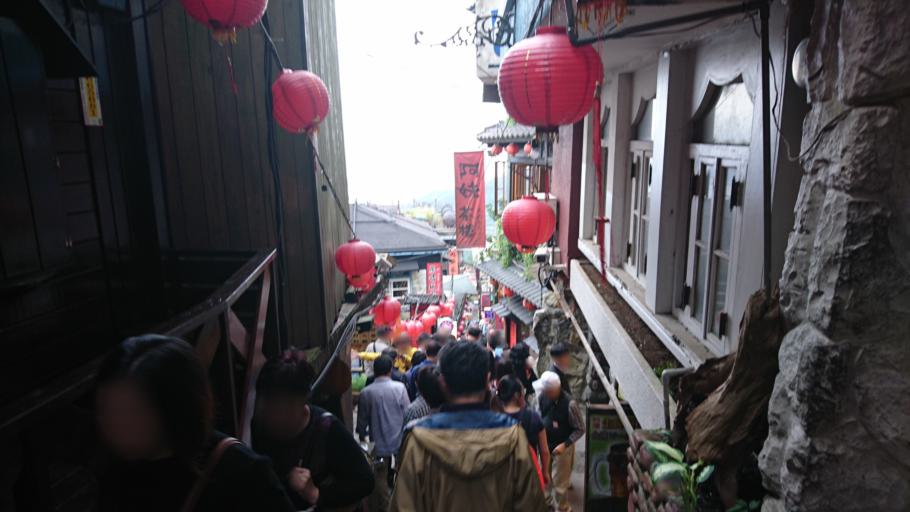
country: TW
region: Taiwan
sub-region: Keelung
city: Keelung
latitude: 25.1084
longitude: 121.8435
